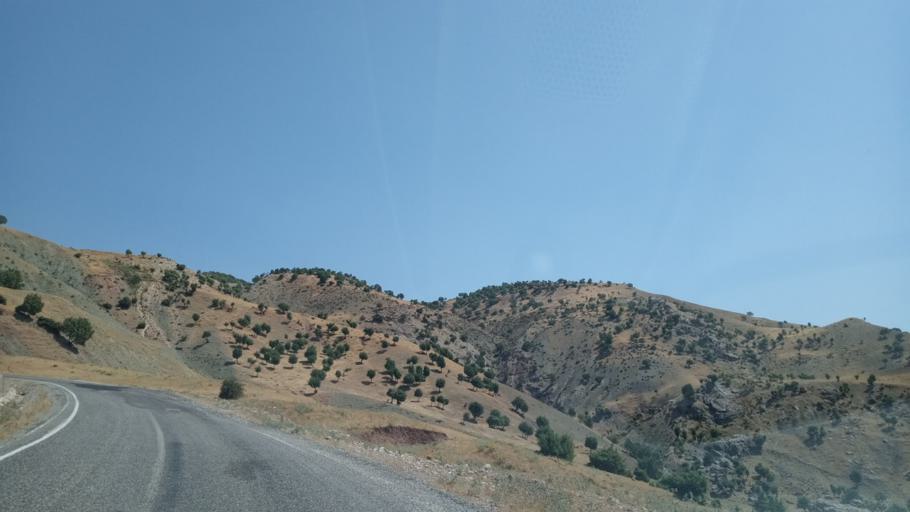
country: TR
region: Siirt
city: Dilektepe
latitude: 38.0647
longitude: 41.8324
